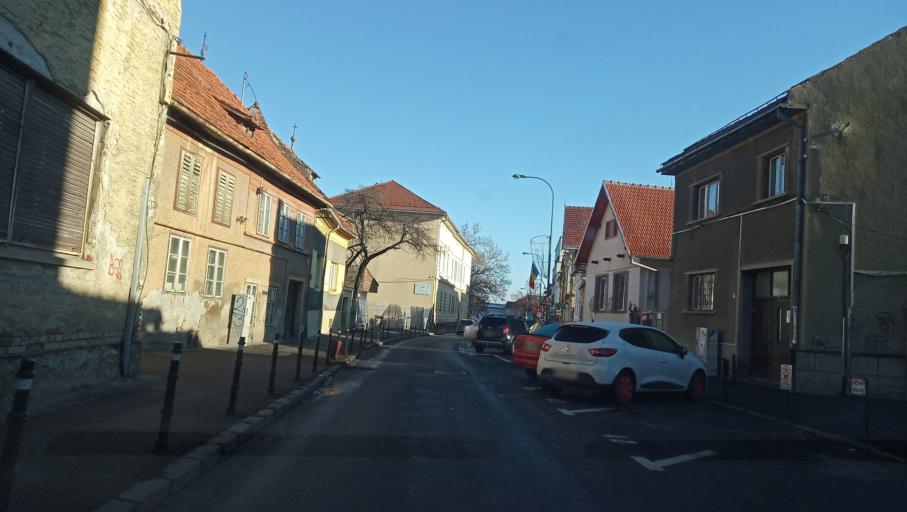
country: RO
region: Brasov
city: Brasov
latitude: 45.6374
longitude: 25.5833
